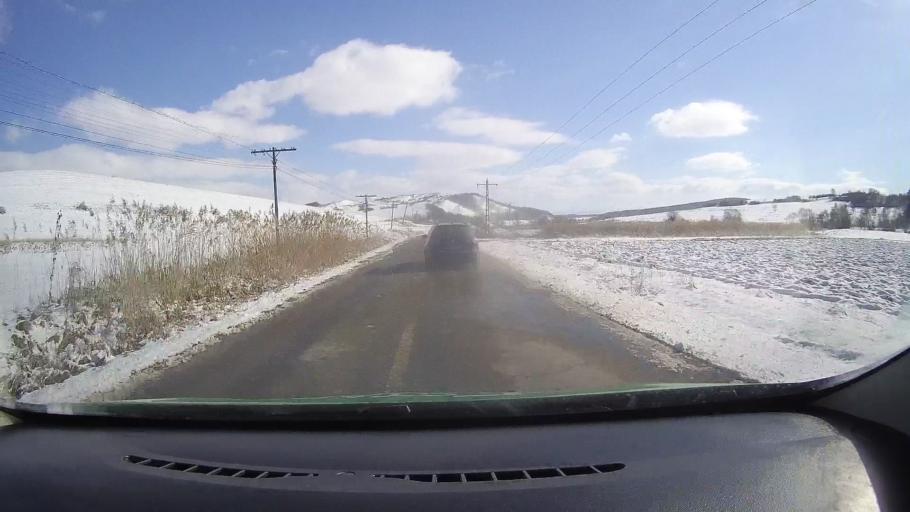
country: RO
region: Sibiu
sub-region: Comuna Altina
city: Altina
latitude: 45.9804
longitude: 24.4606
